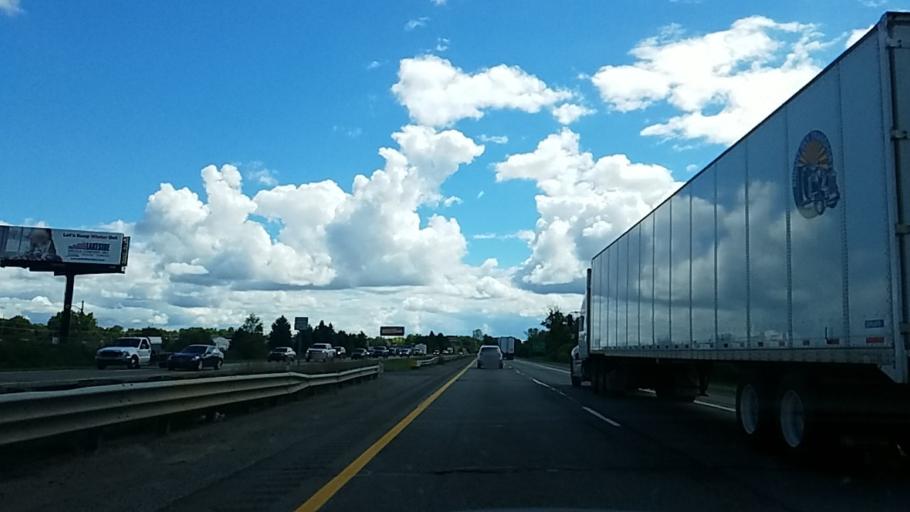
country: US
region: Michigan
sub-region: Livingston County
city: Whitmore Lake
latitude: 42.4145
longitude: -83.7652
